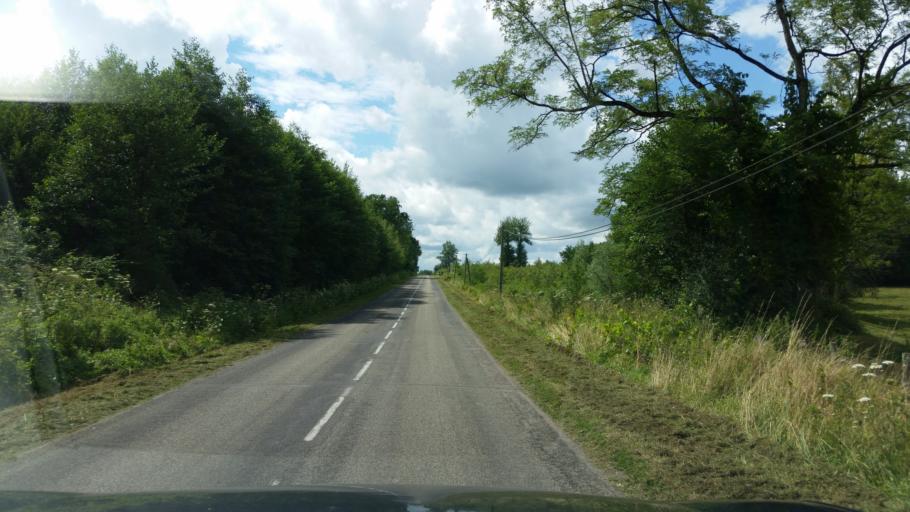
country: FR
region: Franche-Comte
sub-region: Departement du Jura
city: Bletterans
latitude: 46.6910
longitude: 5.3656
